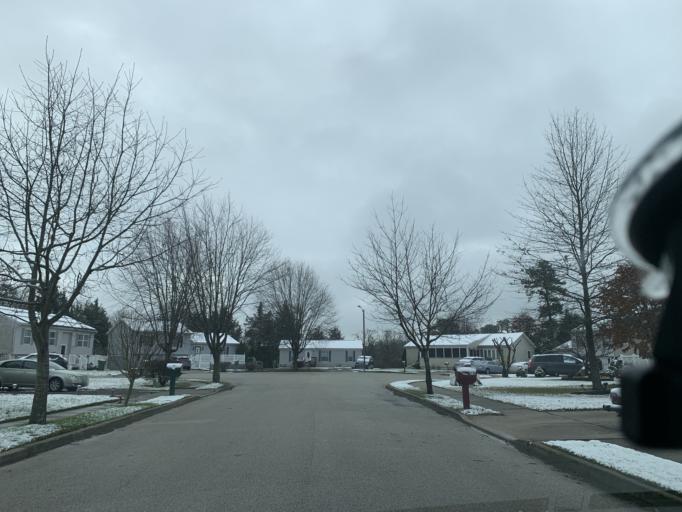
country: US
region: New Jersey
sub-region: Atlantic County
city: Pomona
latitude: 39.4326
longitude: -74.5874
